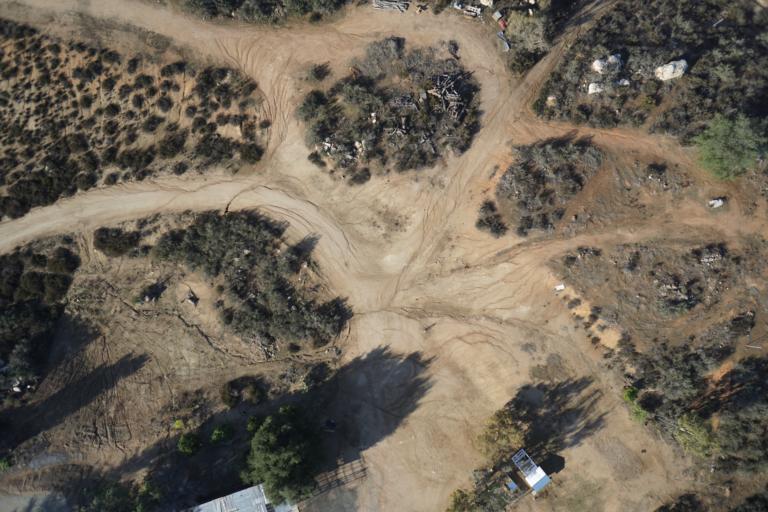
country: US
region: California
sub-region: Riverside County
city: East Hemet
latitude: 33.6122
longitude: -116.9366
